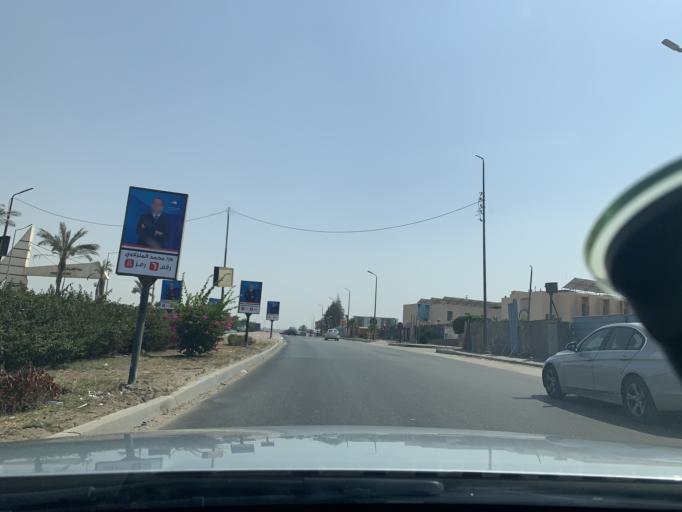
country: EG
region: Muhafazat al Qalyubiyah
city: Al Khankah
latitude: 30.0959
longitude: 31.3828
